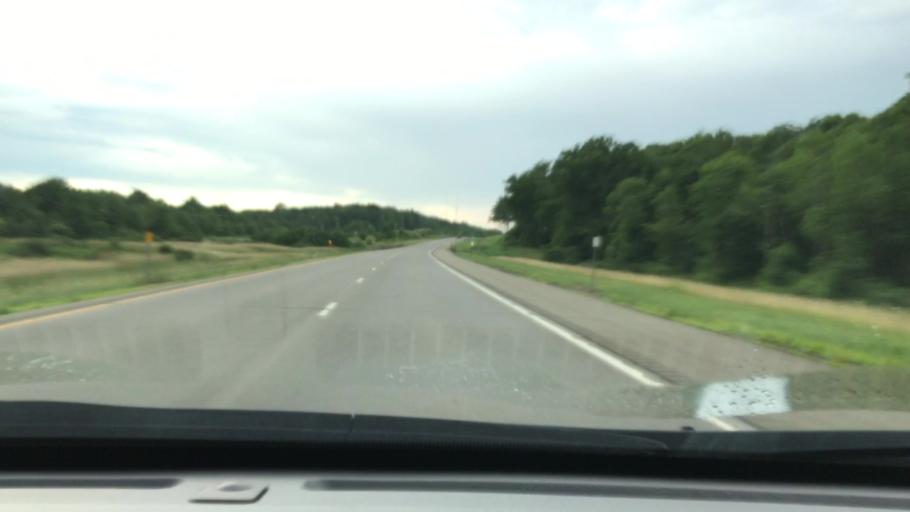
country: US
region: New York
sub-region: Erie County
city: North Boston
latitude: 42.6175
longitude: -78.7622
